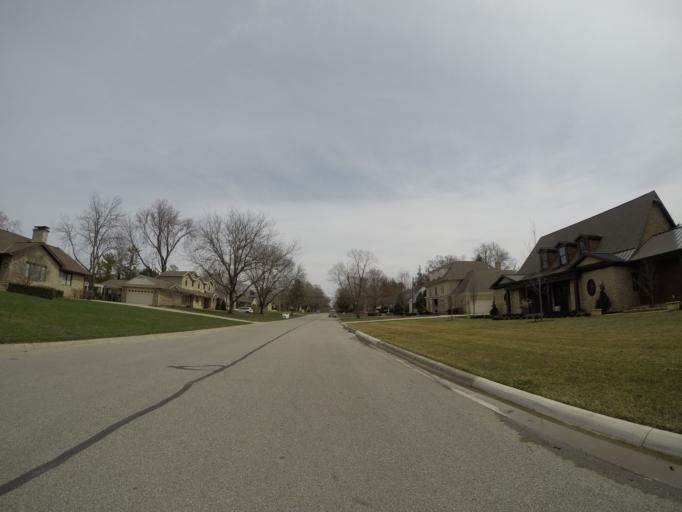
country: US
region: Ohio
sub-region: Franklin County
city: Upper Arlington
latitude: 40.0110
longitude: -83.0798
